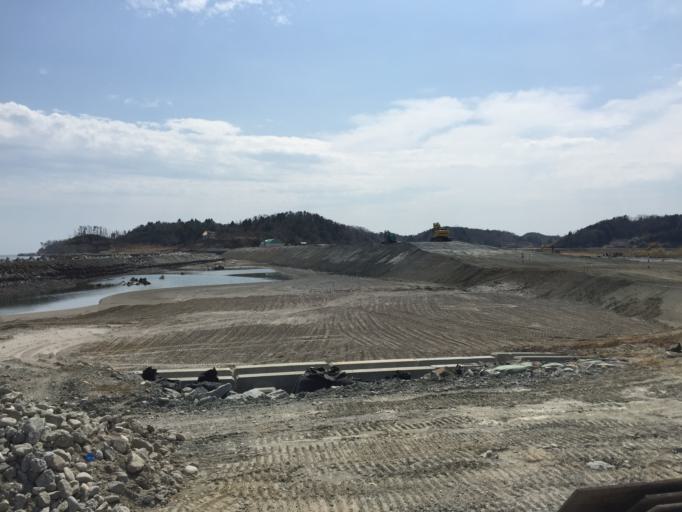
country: JP
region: Fukushima
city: Namie
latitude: 37.7620
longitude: 140.9990
